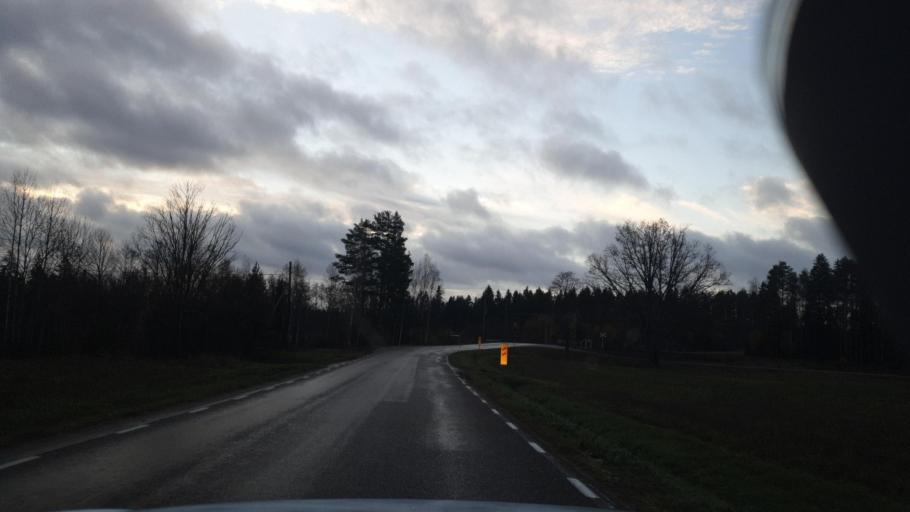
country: SE
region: Vaermland
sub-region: Arvika Kommun
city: Arvika
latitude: 59.6292
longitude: 12.8003
